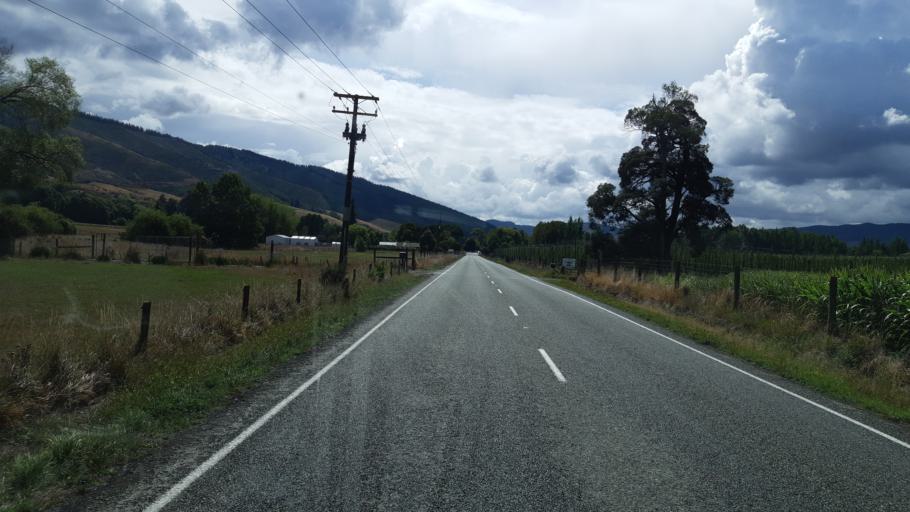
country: NZ
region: Tasman
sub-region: Tasman District
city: Wakefield
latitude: -41.4639
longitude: 172.8094
